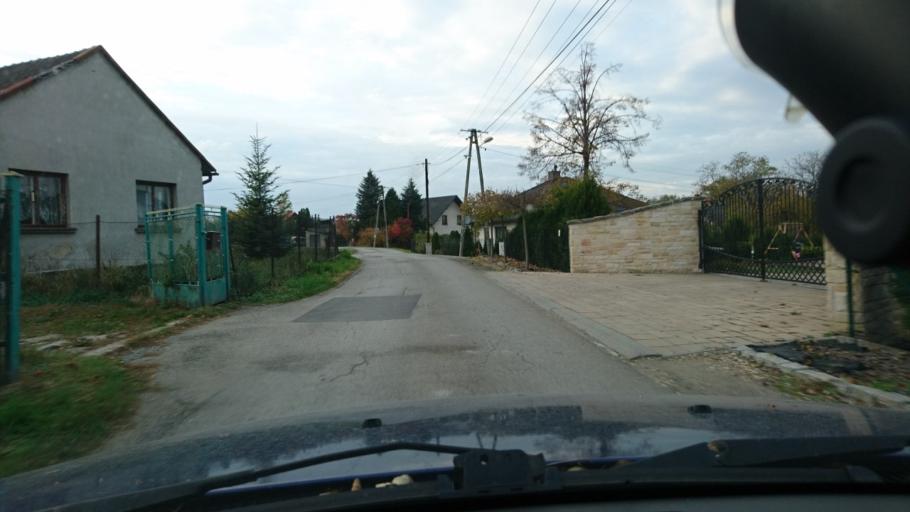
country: PL
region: Silesian Voivodeship
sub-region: Powiat bielski
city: Kozy
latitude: 49.8648
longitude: 19.1578
